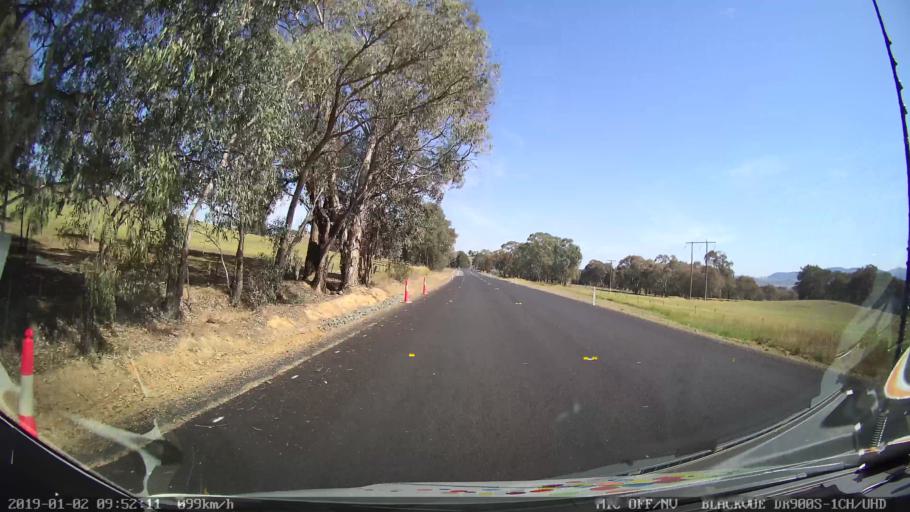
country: AU
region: New South Wales
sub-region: Tumut Shire
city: Tumut
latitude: -35.2638
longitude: 148.2084
